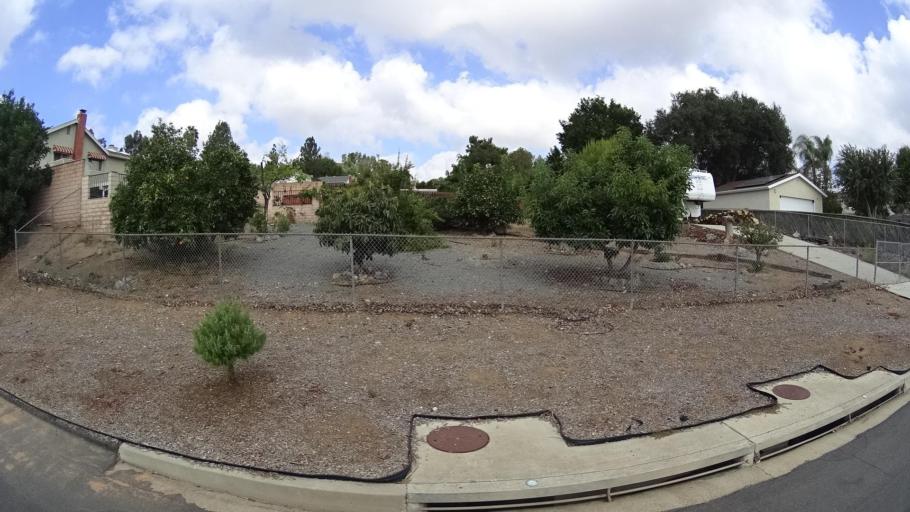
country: US
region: California
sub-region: San Diego County
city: Rancho San Diego
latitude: 32.7664
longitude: -116.9177
